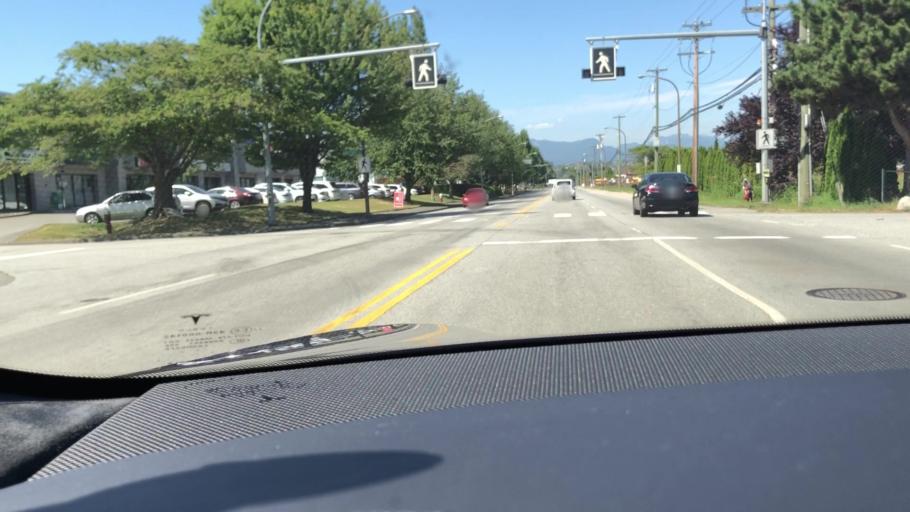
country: CA
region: British Columbia
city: Richmond
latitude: 49.1794
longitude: -123.0692
